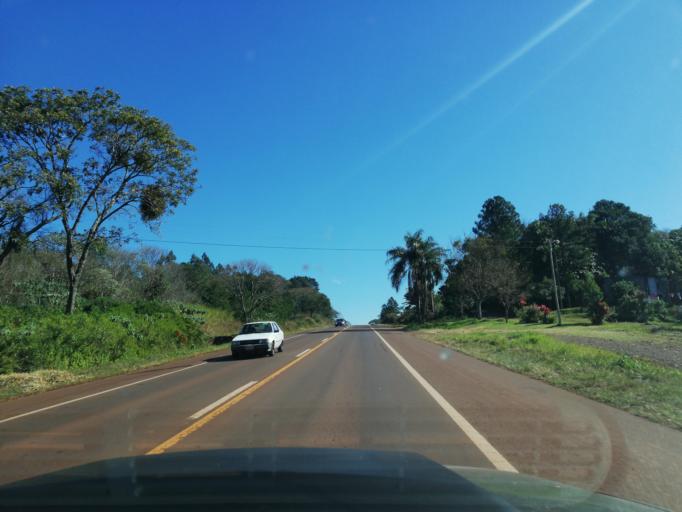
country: AR
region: Misiones
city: Aristobulo del Valle
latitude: -27.0874
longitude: -54.8518
